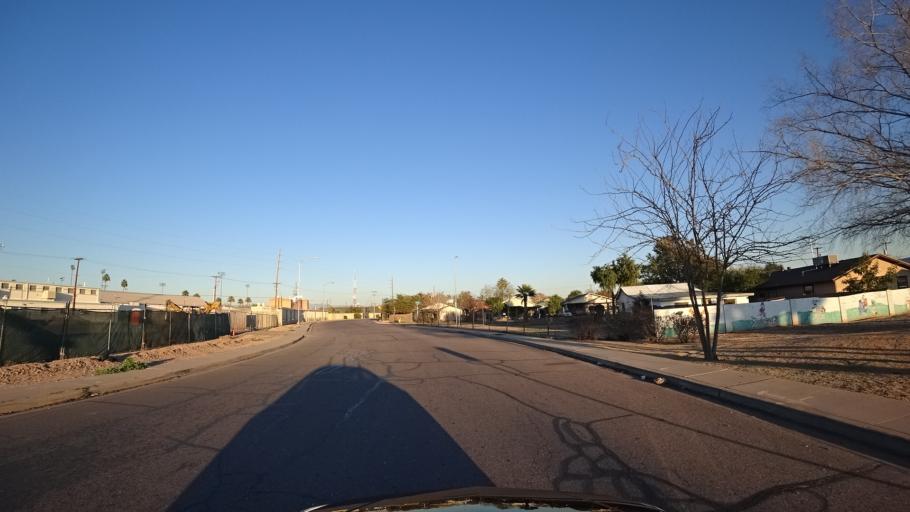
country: US
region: Arizona
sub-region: Maricopa County
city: Mesa
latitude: 33.4254
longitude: -111.8312
